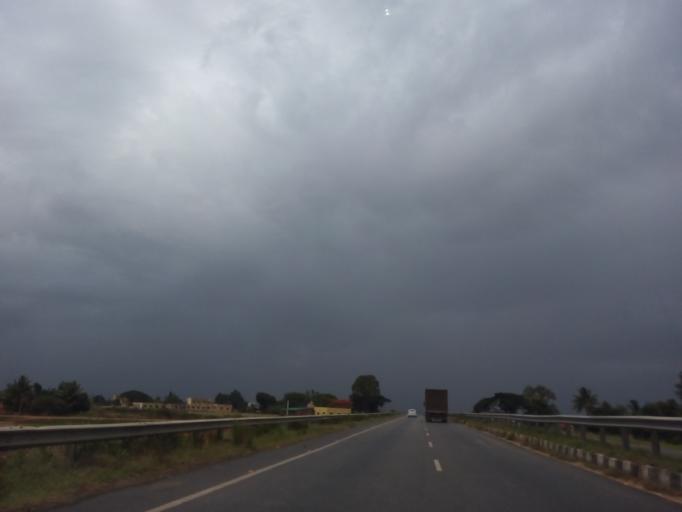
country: IN
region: Karnataka
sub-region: Davanagere
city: Harihar
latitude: 14.4562
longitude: 75.8655
